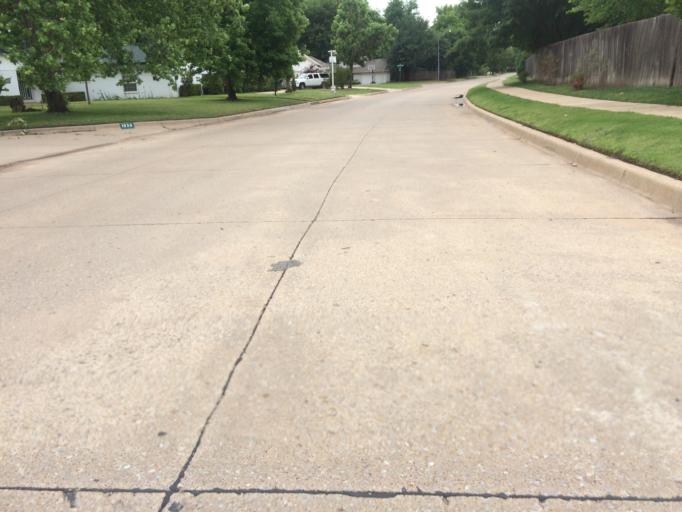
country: US
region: Oklahoma
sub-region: Cleveland County
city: Norman
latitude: 35.1873
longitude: -97.4561
